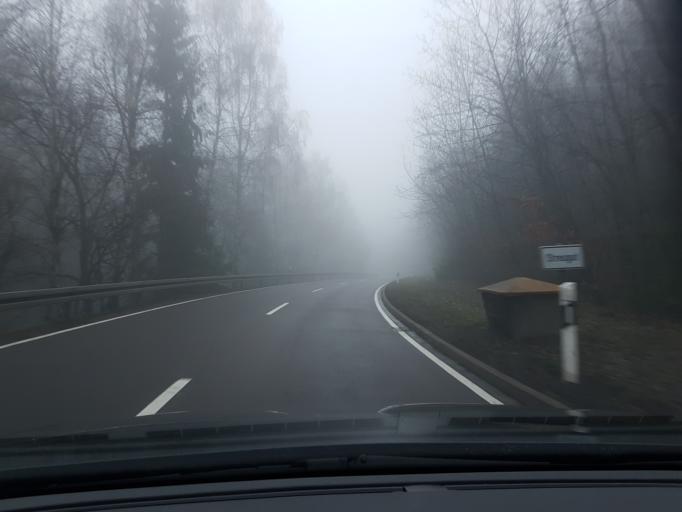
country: DE
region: Saxony-Anhalt
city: Stolberg
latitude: 51.5586
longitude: 11.0116
